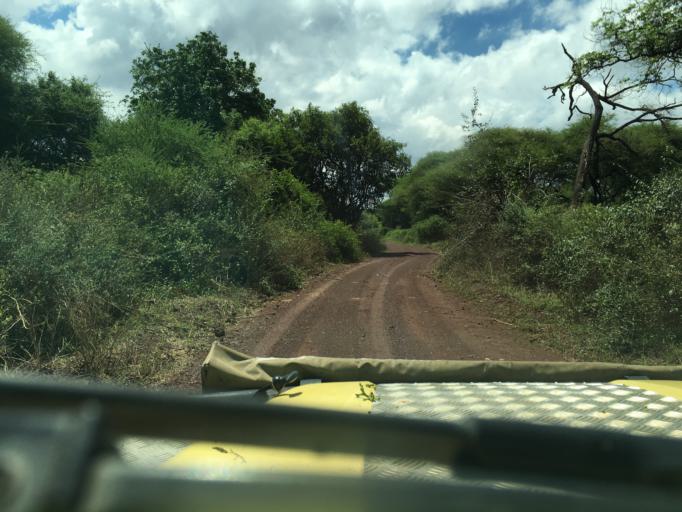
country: TZ
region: Arusha
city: Mto wa Mbu
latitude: -3.4220
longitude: 35.8143
